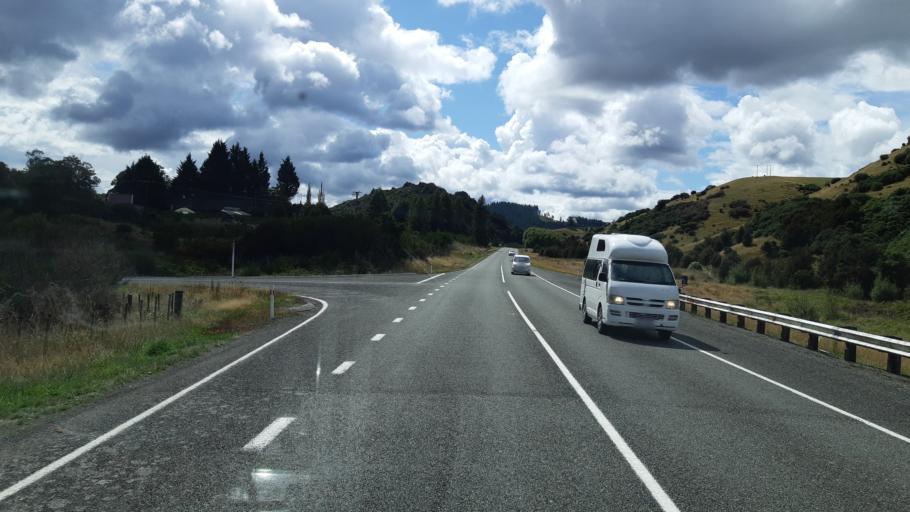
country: NZ
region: Tasman
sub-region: Tasman District
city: Wakefield
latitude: -41.6487
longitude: 172.6512
